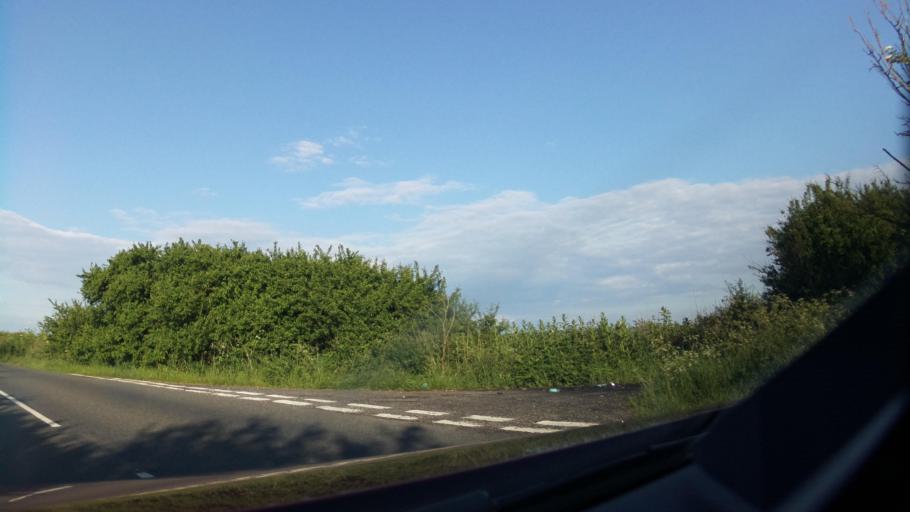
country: GB
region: England
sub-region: Lincolnshire
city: Navenby
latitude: 53.1007
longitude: -0.6115
